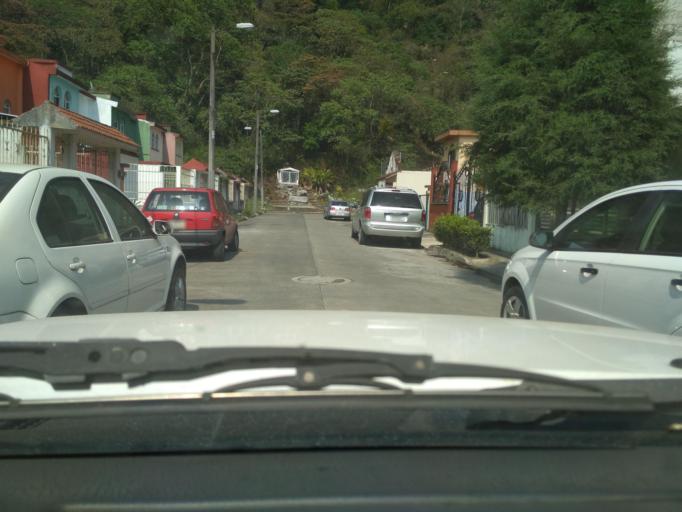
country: MX
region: Veracruz
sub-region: Mariano Escobedo
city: Palmira
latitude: 18.8739
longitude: -97.0969
